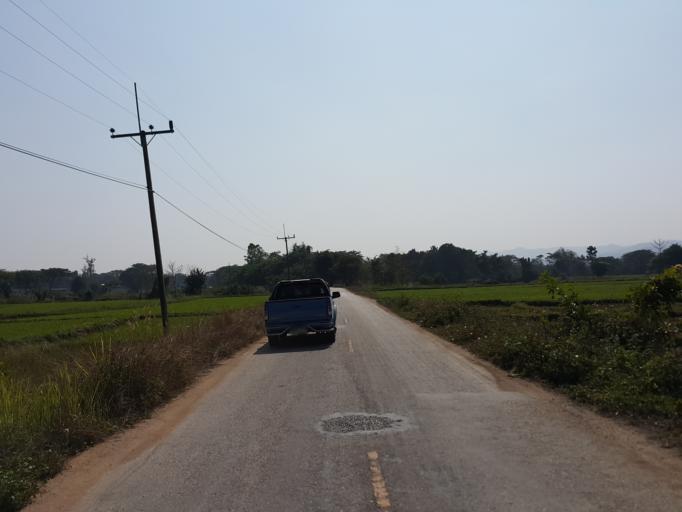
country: TH
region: Lampang
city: Wang Nuea
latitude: 19.0551
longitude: 99.6240
